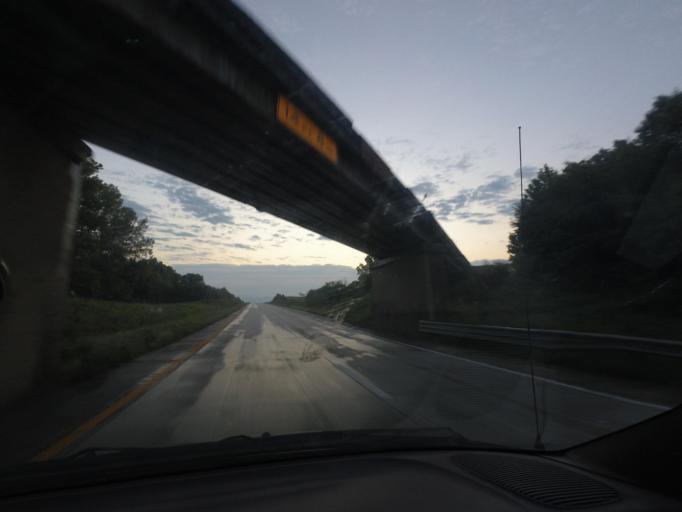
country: US
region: Missouri
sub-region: Macon County
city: Macon
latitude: 39.7555
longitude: -92.6098
